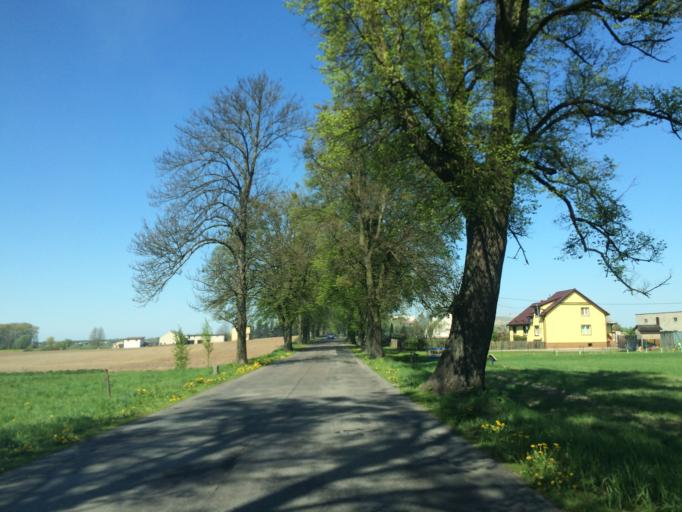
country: PL
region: Warmian-Masurian Voivodeship
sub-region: Powiat nowomiejski
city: Biskupiec
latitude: 53.4962
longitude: 19.3797
